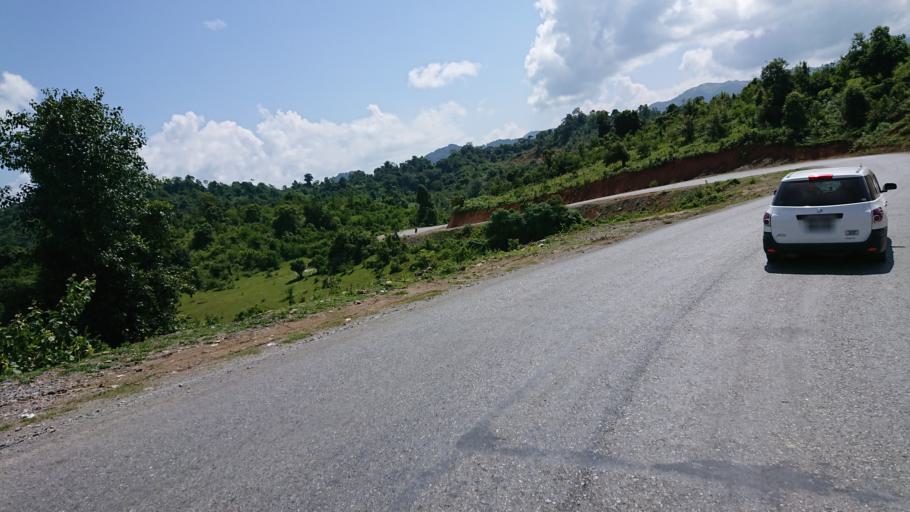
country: MM
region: Shan
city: Taunggyi
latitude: 20.8183
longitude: 97.3129
